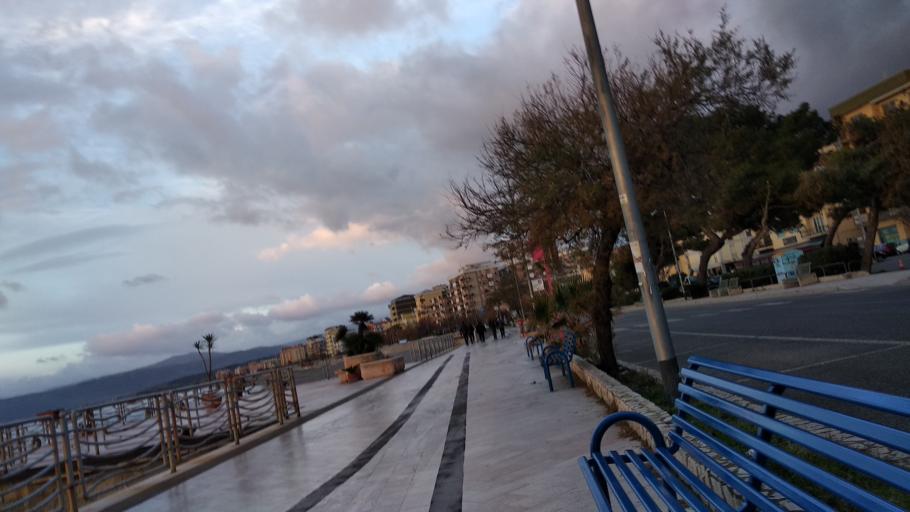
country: IT
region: Calabria
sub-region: Provincia di Catanzaro
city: Barone
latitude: 38.8267
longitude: 16.6275
